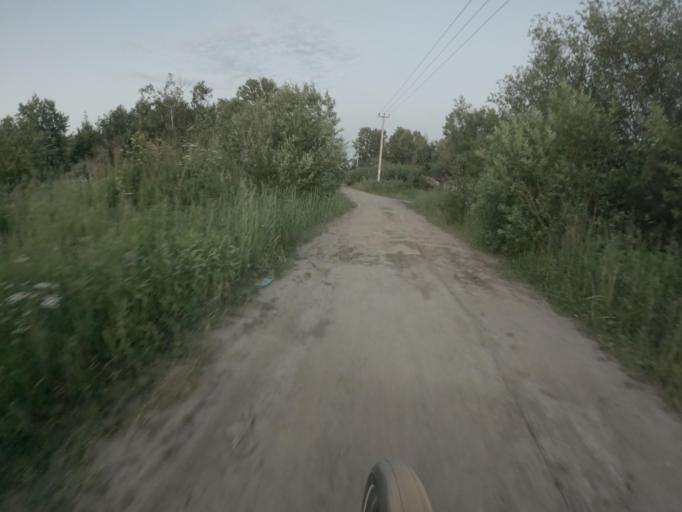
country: RU
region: Leningrad
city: Imeni Sverdlova
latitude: 59.7807
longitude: 30.6895
